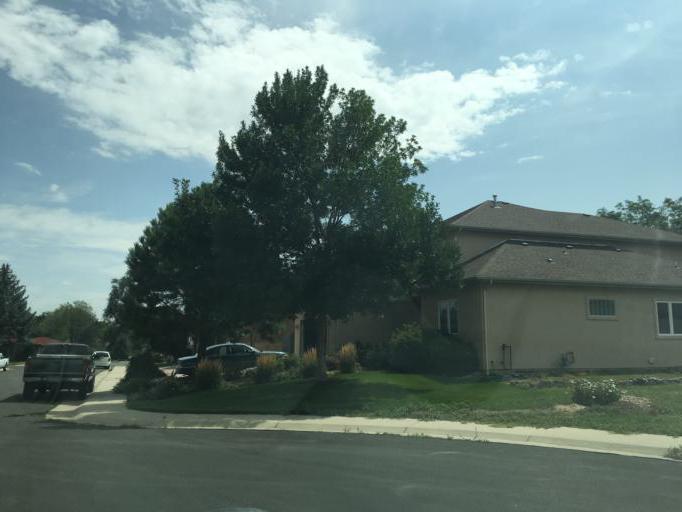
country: US
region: Colorado
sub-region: Adams County
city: Aurora
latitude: 39.7329
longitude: -104.8017
